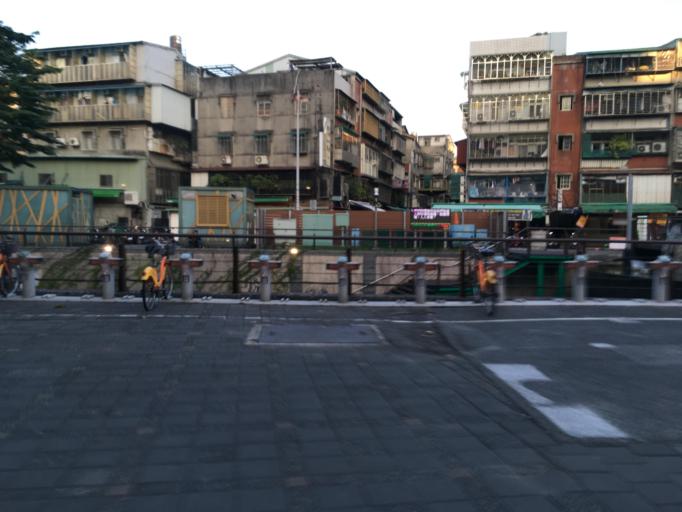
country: TW
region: Taipei
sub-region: Taipei
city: Banqiao
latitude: 25.0462
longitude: 121.4537
